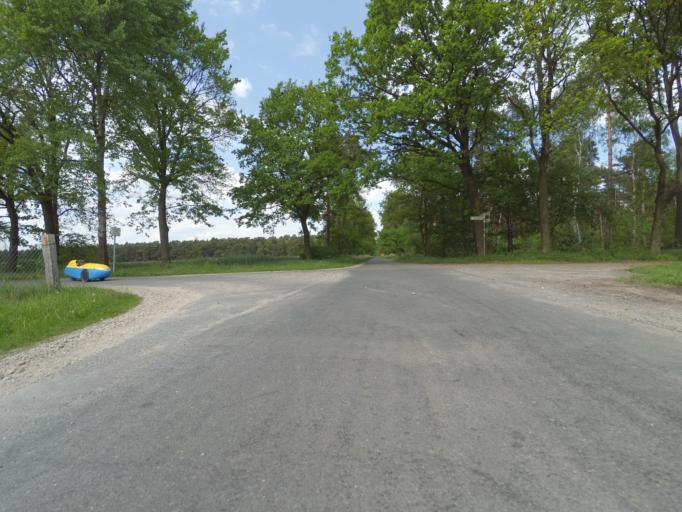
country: DE
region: Lower Saxony
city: Adelheidsdorf
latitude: 52.5643
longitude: 10.0339
